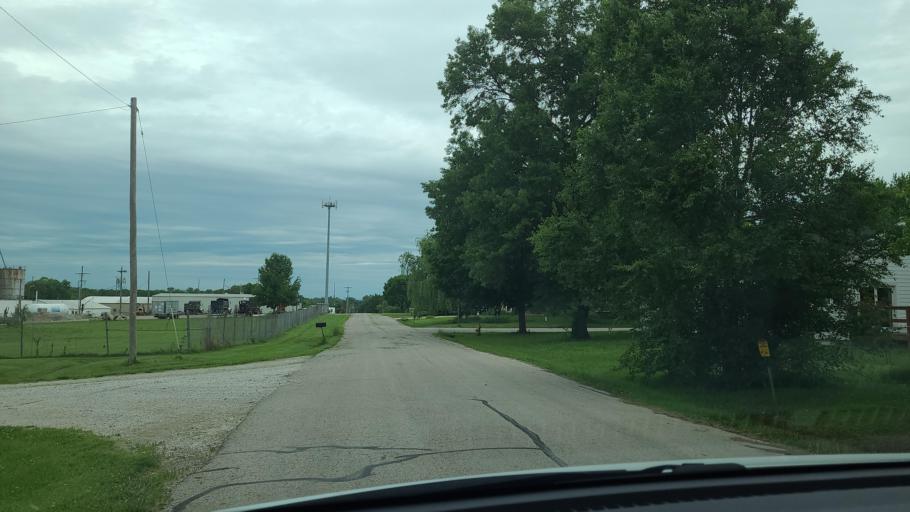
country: US
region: Kansas
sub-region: Douglas County
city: Lawrence
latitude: 38.9463
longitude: -95.2258
